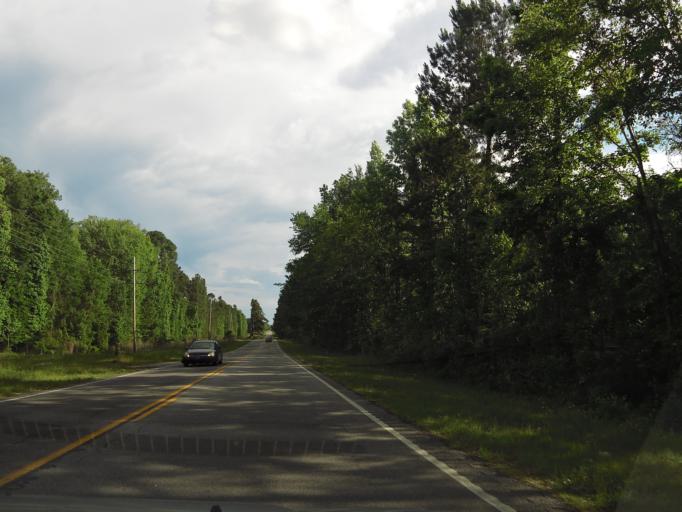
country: US
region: South Carolina
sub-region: Hampton County
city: Estill
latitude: 32.7746
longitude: -81.2409
